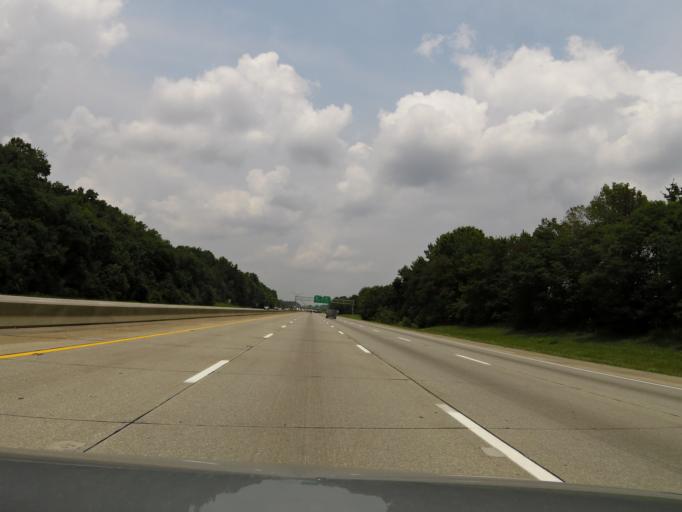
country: US
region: Kentucky
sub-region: Jefferson County
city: Heritage Creek
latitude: 38.1032
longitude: -85.7010
